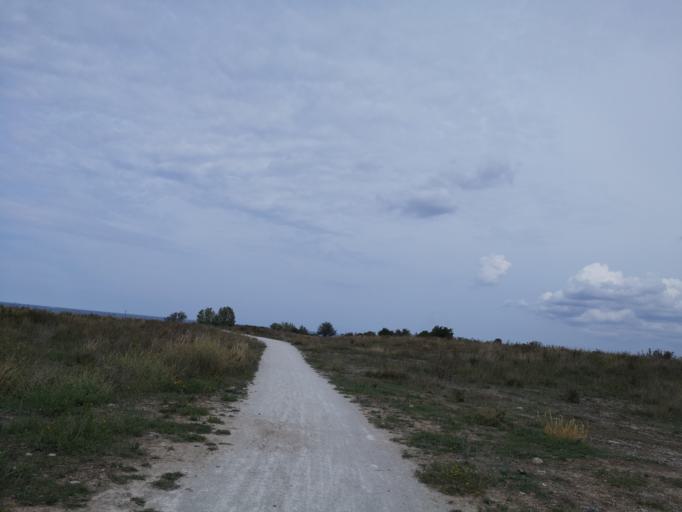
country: SE
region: Gotland
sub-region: Gotland
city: Vibble
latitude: 57.6167
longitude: 18.2615
